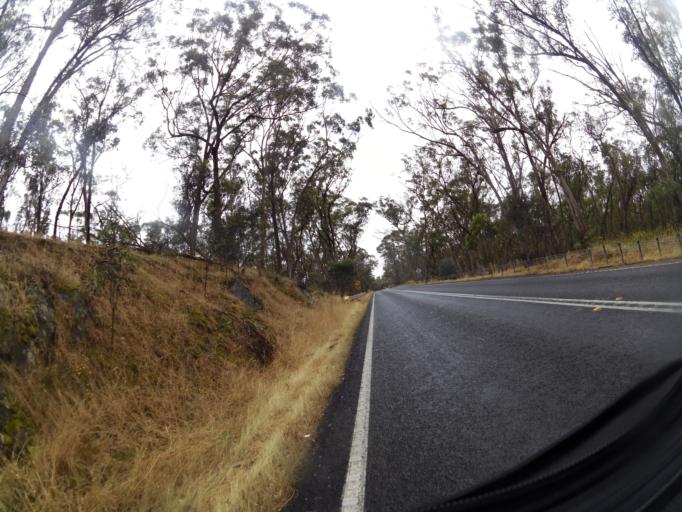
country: AU
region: Victoria
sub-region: Mount Alexander
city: Castlemaine
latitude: -37.1052
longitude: 144.1049
